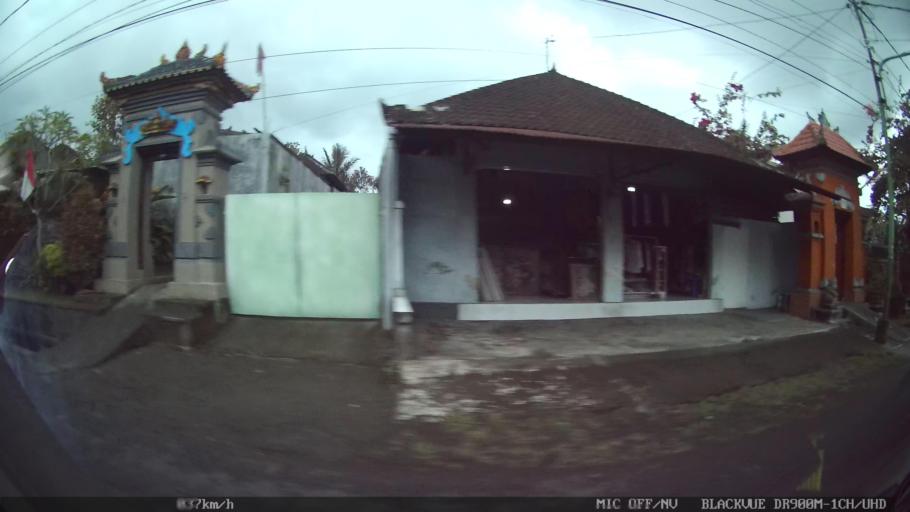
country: ID
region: Bali
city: Banjar Sempidi
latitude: -8.5225
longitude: 115.1907
